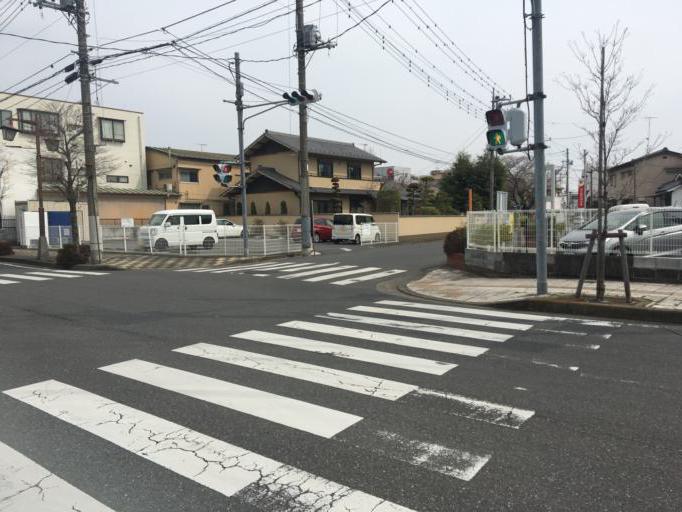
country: JP
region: Saitama
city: Gyoda
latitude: 36.1414
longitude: 139.4594
